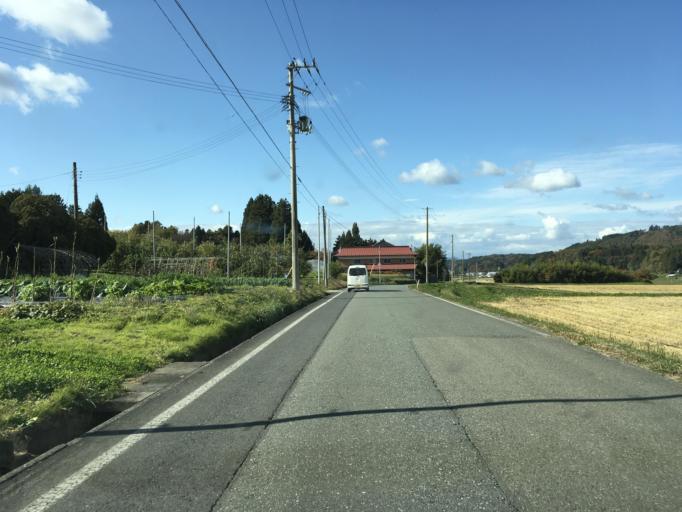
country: JP
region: Iwate
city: Ichinoseki
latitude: 38.9496
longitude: 141.3944
